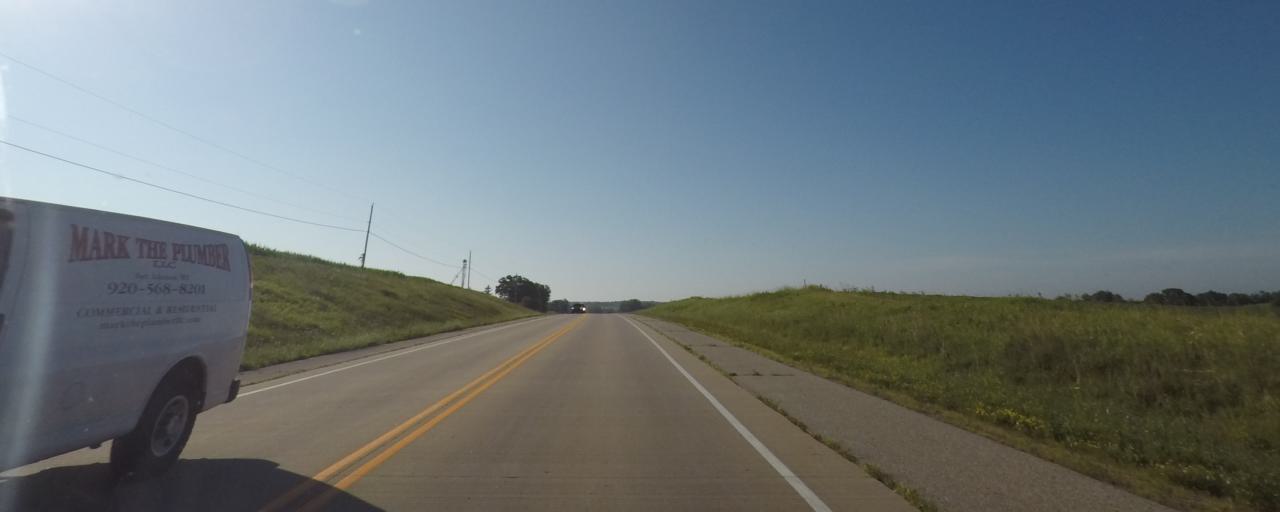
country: US
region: Wisconsin
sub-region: Jefferson County
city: Lake Ripley
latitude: 42.9840
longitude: -88.9700
